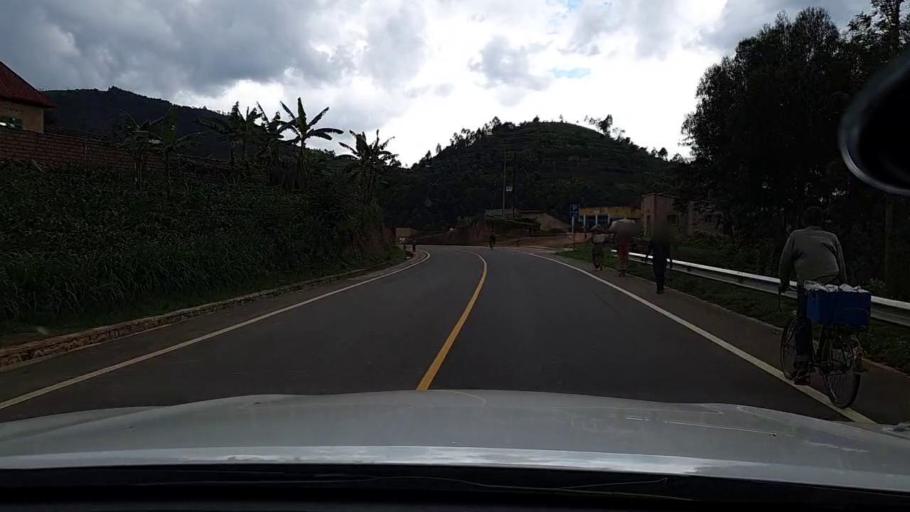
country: RW
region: Northern Province
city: Byumba
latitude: -1.6474
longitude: 29.9205
